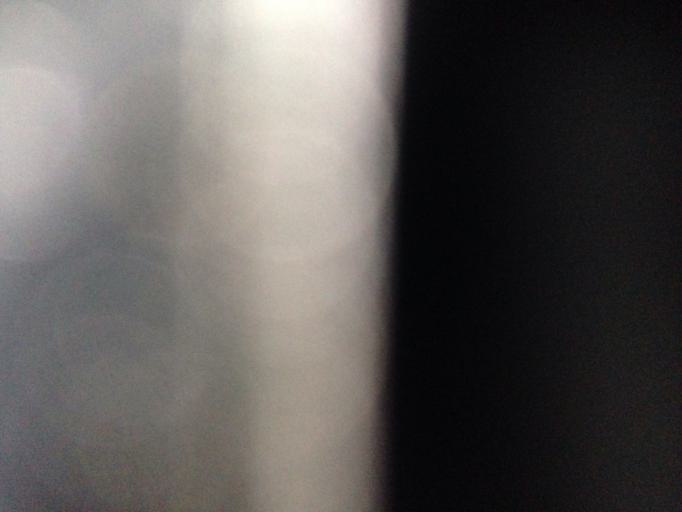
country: CO
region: Valle del Cauca
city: Cali
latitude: 3.4566
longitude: -76.5745
